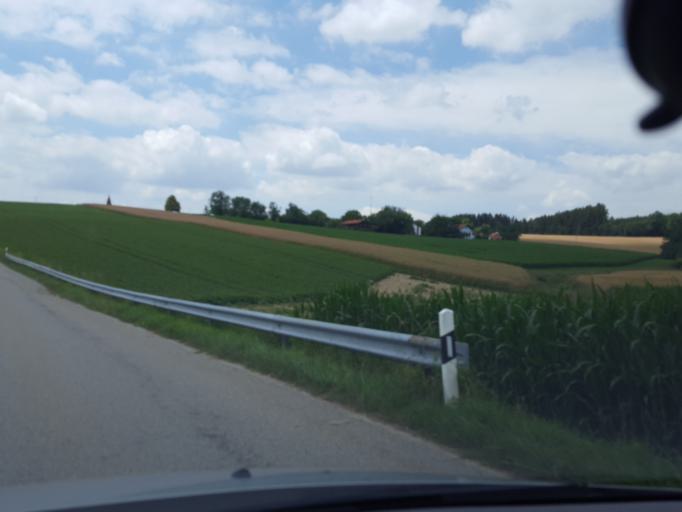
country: DE
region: Bavaria
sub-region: Upper Bavaria
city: Egglkofen
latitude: 48.3946
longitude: 12.4630
